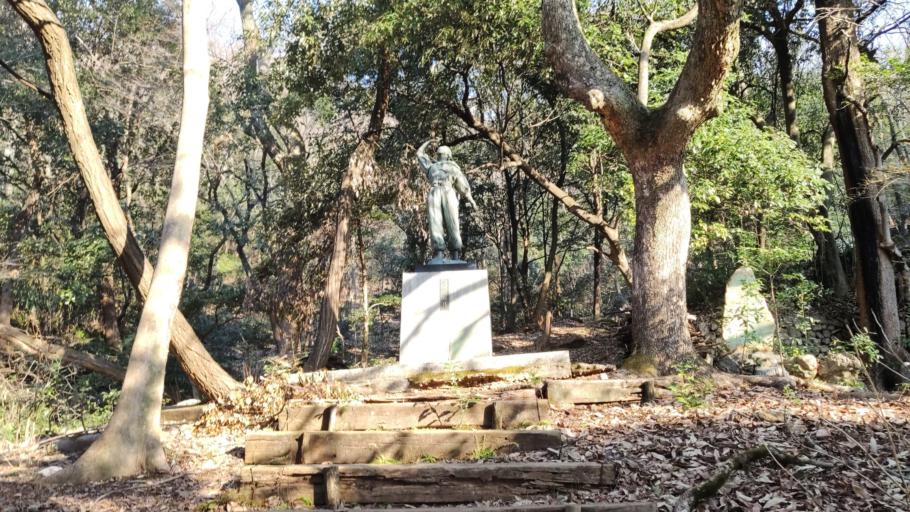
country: JP
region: Gifu
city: Gifu-shi
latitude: 35.4194
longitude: 136.7709
